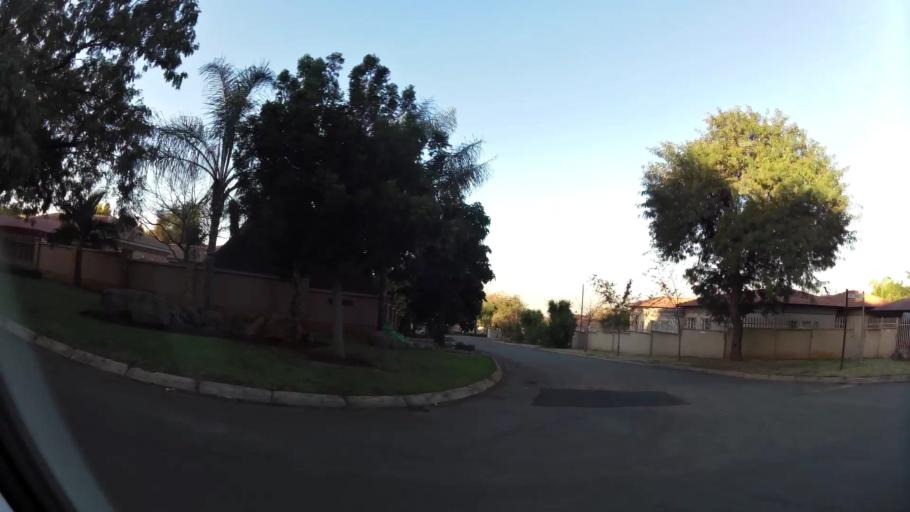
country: ZA
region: North-West
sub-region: Bojanala Platinum District Municipality
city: Rustenburg
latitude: -25.7092
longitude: 27.2329
